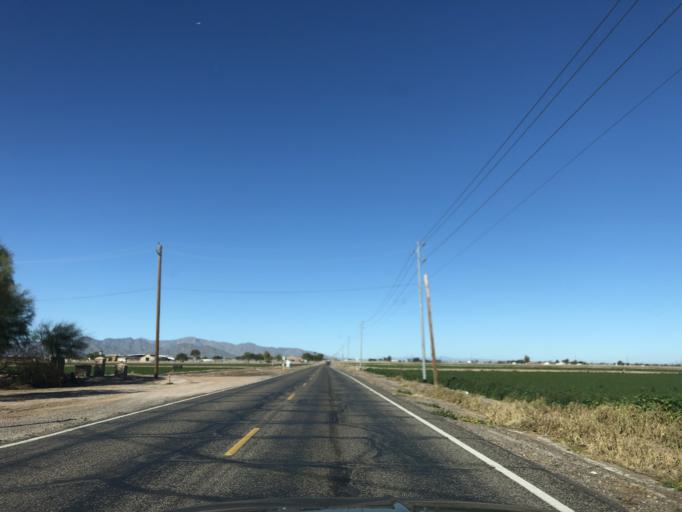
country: US
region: Arizona
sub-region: Maricopa County
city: Buckeye
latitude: 33.3832
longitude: -112.5042
